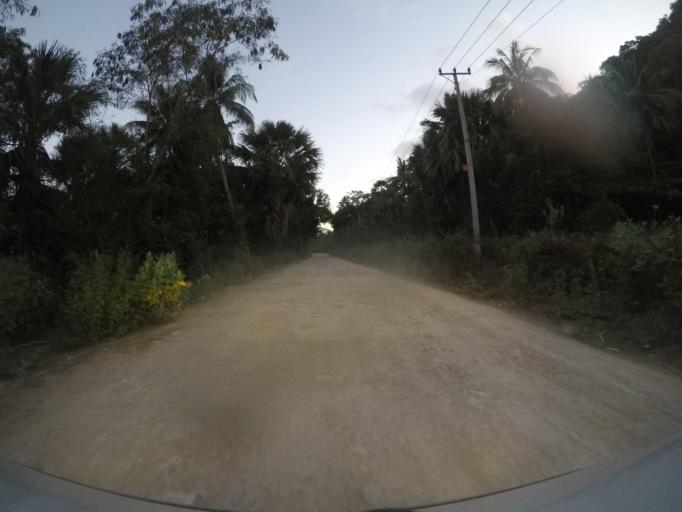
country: TL
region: Viqueque
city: Viqueque
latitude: -8.7932
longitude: 126.6244
